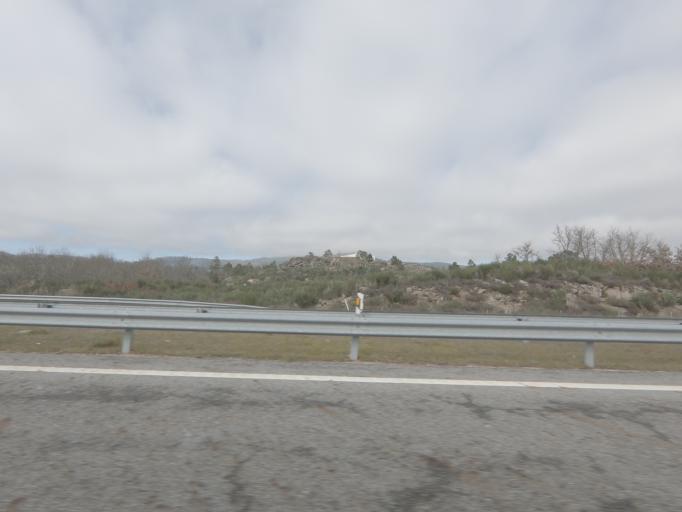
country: PT
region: Vila Real
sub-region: Chaves
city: Chaves
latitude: 41.7627
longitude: -7.5011
